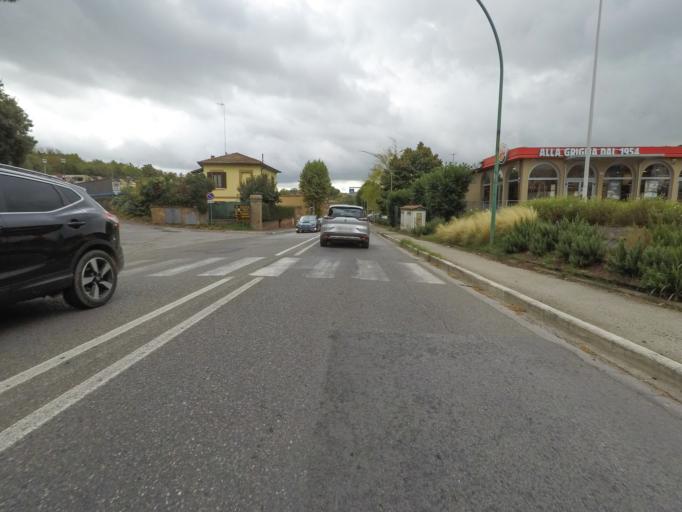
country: IT
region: Tuscany
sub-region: Provincia di Siena
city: Siena
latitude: 43.3176
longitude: 11.3537
